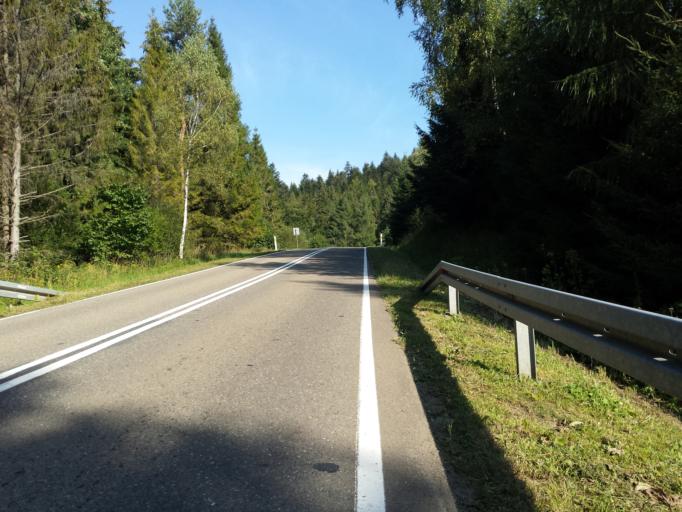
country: PL
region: Subcarpathian Voivodeship
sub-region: Powiat leski
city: Cisna
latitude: 49.2352
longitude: 22.3015
